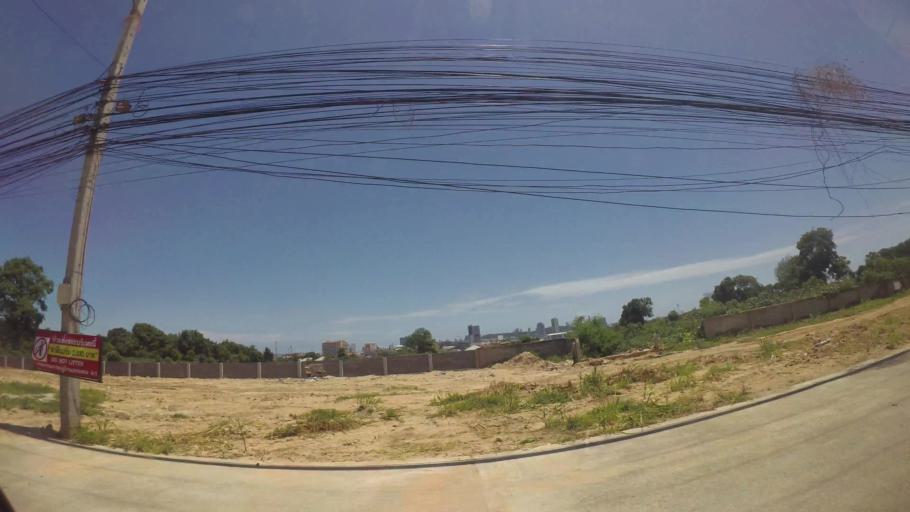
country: TH
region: Chon Buri
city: Phatthaya
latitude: 12.9140
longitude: 100.9017
